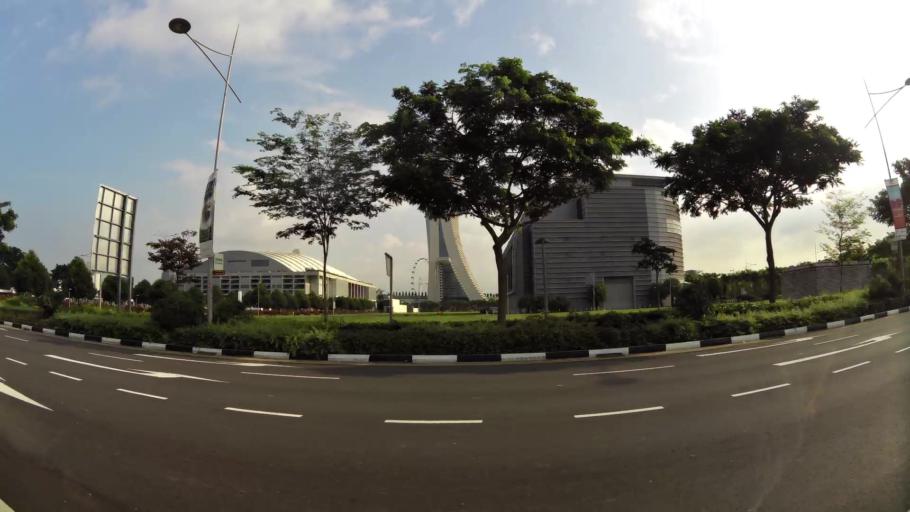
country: SG
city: Singapore
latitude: 1.2784
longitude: 103.8578
